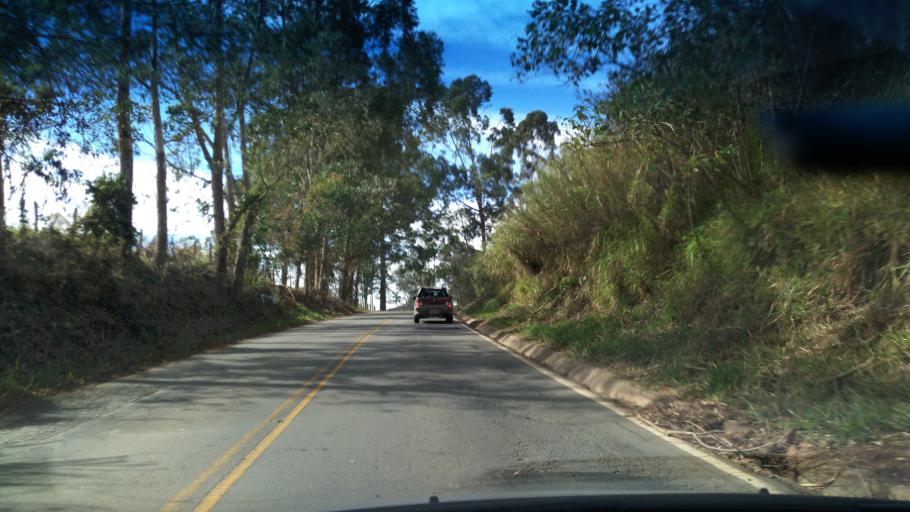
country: BR
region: Minas Gerais
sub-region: Andradas
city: Andradas
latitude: -22.0662
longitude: -46.4628
